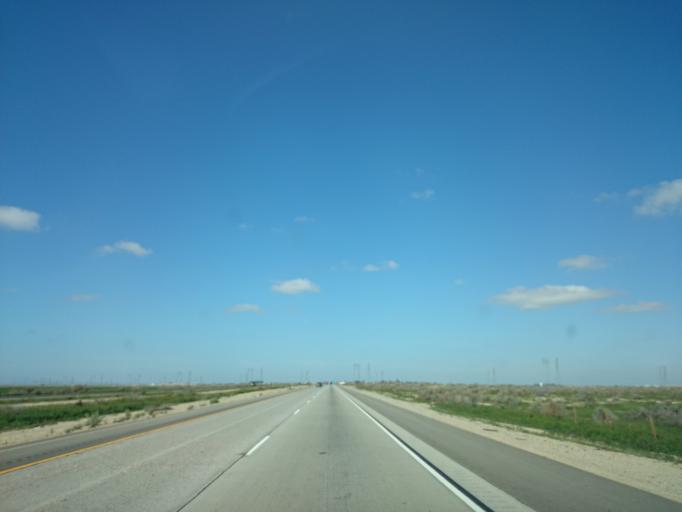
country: US
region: California
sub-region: Kern County
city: Buttonwillow
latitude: 35.3794
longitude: -119.3700
